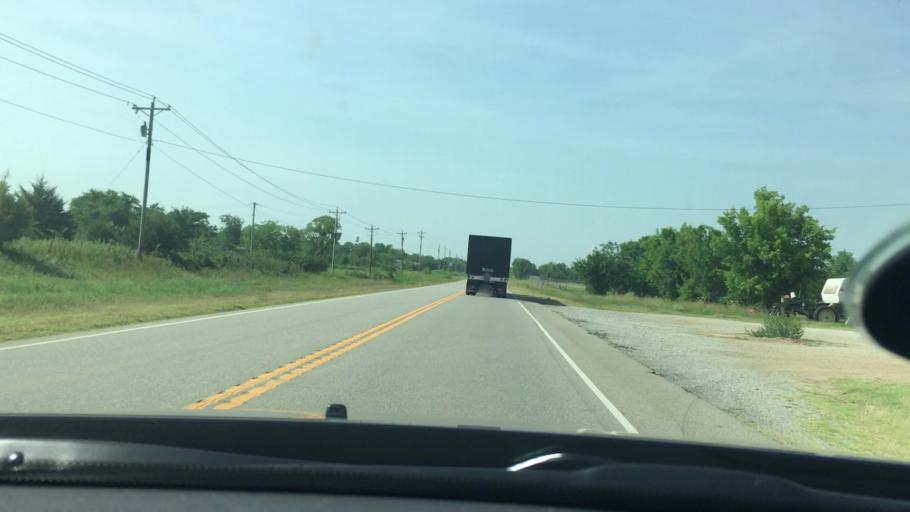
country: US
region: Oklahoma
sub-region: Coal County
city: Coalgate
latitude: 34.4814
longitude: -96.2183
